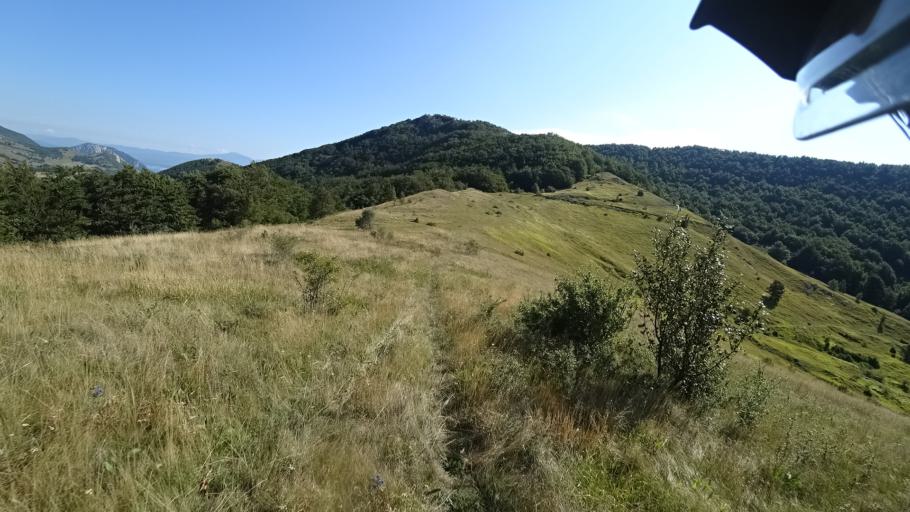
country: HR
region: Zadarska
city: Gracac
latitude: 44.2811
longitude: 16.0880
